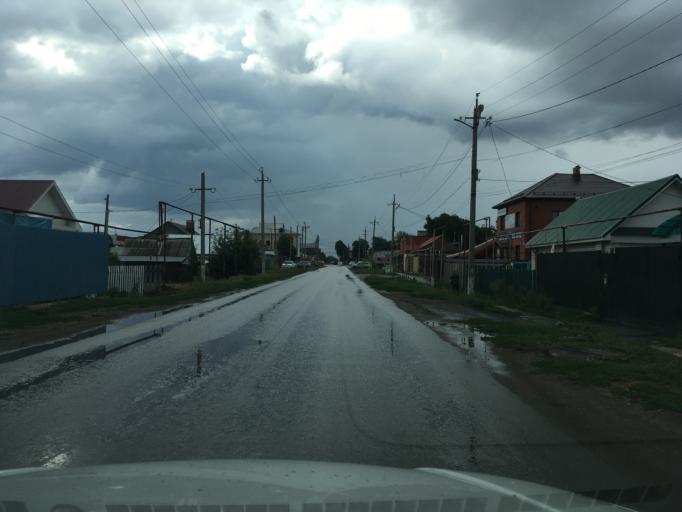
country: RU
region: Samara
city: Bezenchuk
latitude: 52.9802
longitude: 49.4352
